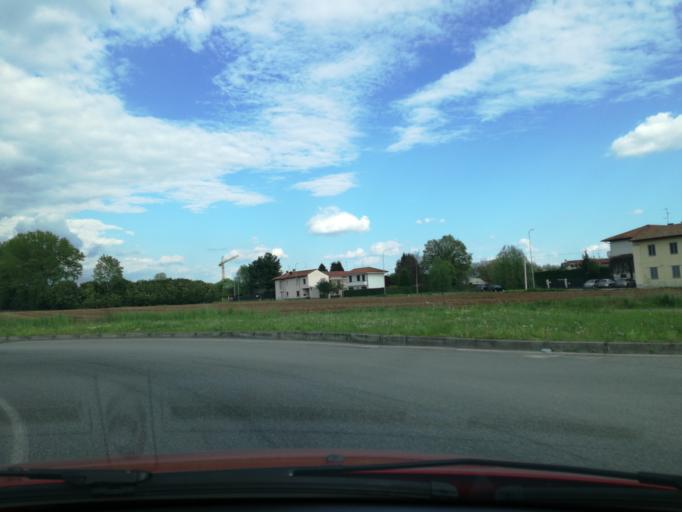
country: IT
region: Lombardy
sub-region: Provincia di Monza e Brianza
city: Albiate
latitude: 45.6505
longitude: 9.2394
